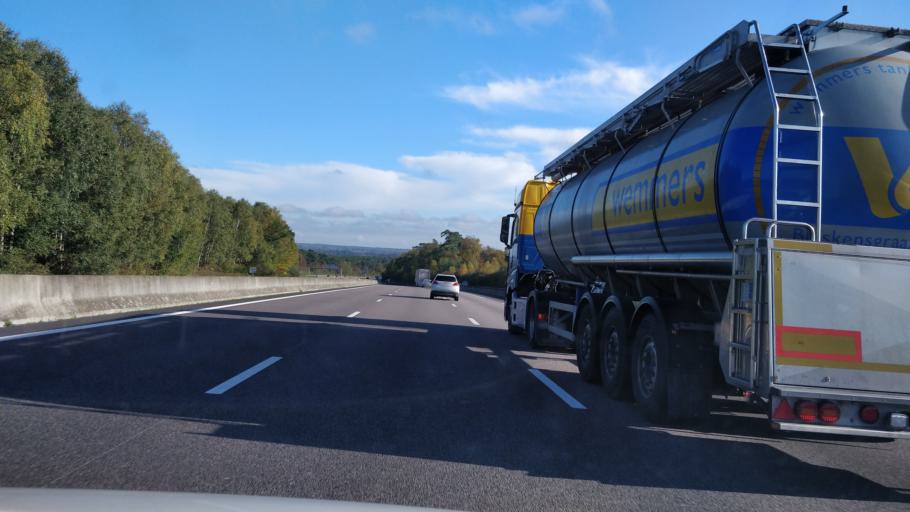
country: FR
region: Haute-Normandie
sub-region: Departement de la Seine-Maritime
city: Cleon
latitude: 49.3436
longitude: 1.0504
